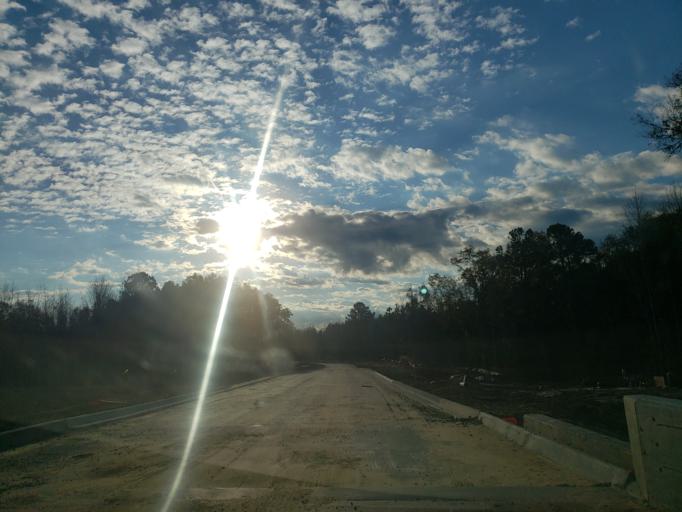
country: US
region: Georgia
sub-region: Chatham County
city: Pooler
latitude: 32.1286
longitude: -81.2465
